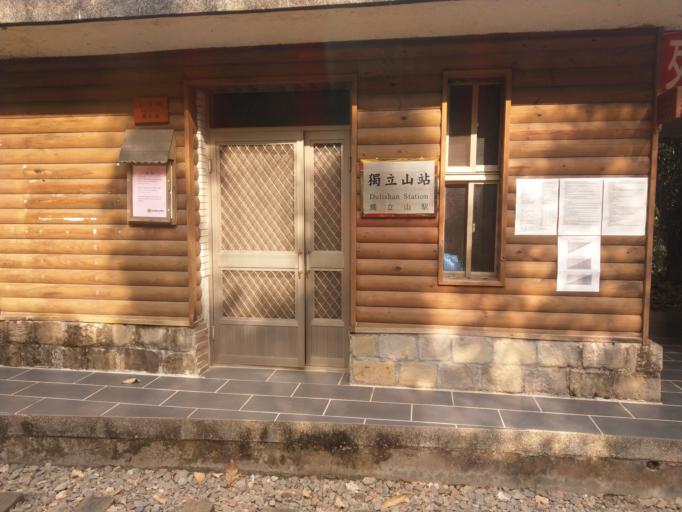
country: TW
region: Taiwan
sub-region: Chiayi
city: Jiayi Shi
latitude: 23.5386
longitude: 120.6074
